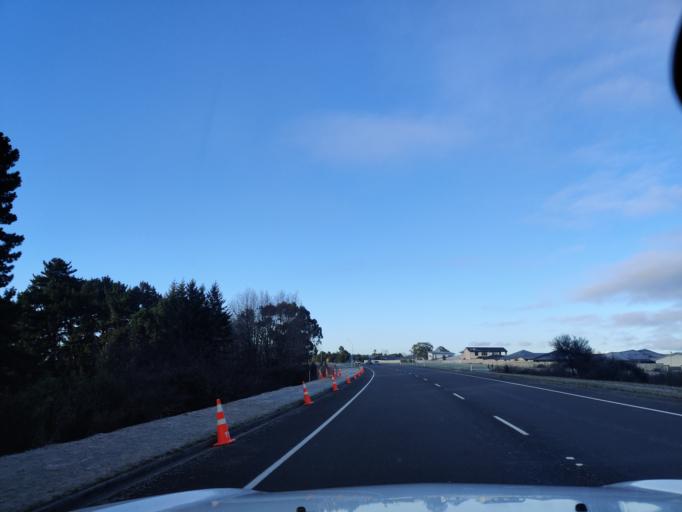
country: NZ
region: Waikato
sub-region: Taupo District
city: Taupo
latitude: -38.7337
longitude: 176.0722
